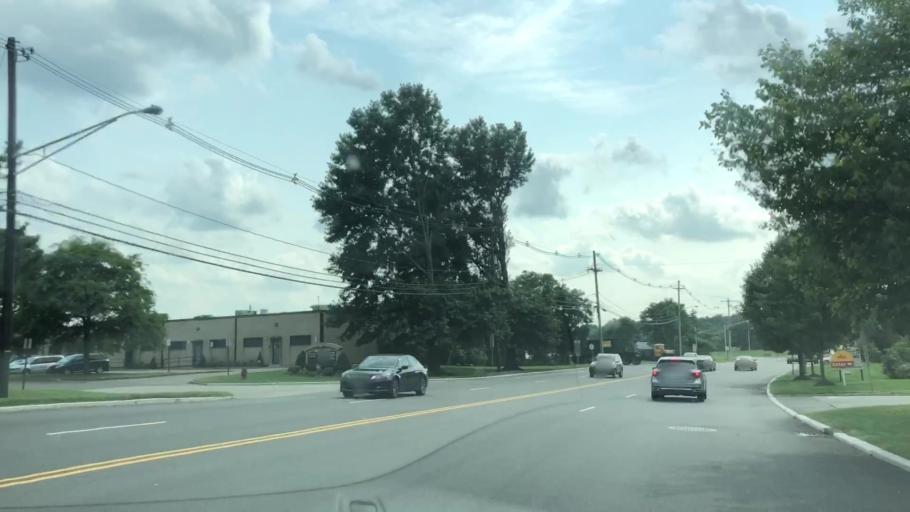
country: US
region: New Jersey
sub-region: Morris County
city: East Hanover
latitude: 40.8507
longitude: -74.3492
